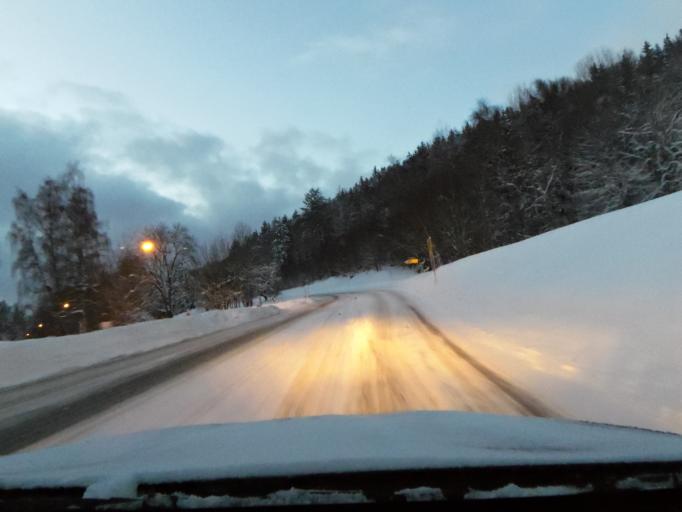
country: DE
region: Bavaria
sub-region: Lower Bavaria
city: Spiegelau
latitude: 48.9130
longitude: 13.3343
